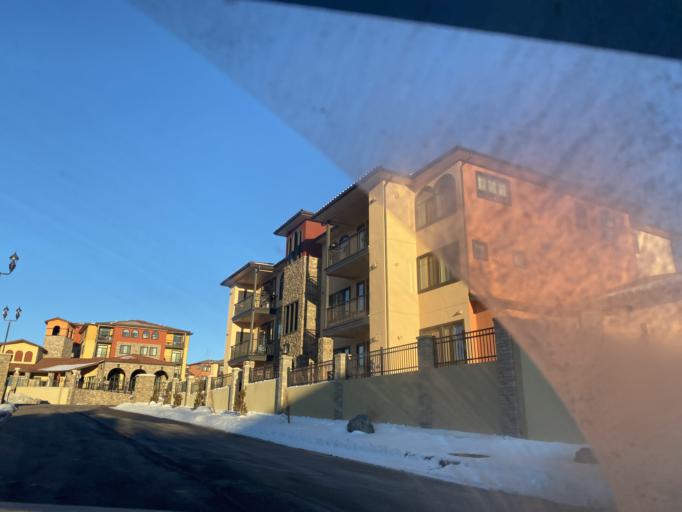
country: US
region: Colorado
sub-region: El Paso County
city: Black Forest
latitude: 38.9653
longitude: -104.7447
